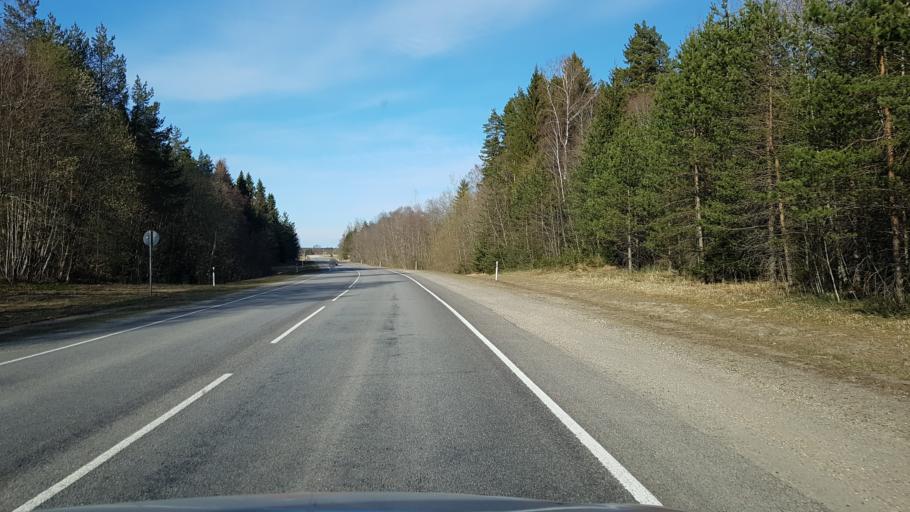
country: EE
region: Ida-Virumaa
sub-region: Johvi vald
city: Johvi
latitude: 59.1381
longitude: 27.3471
